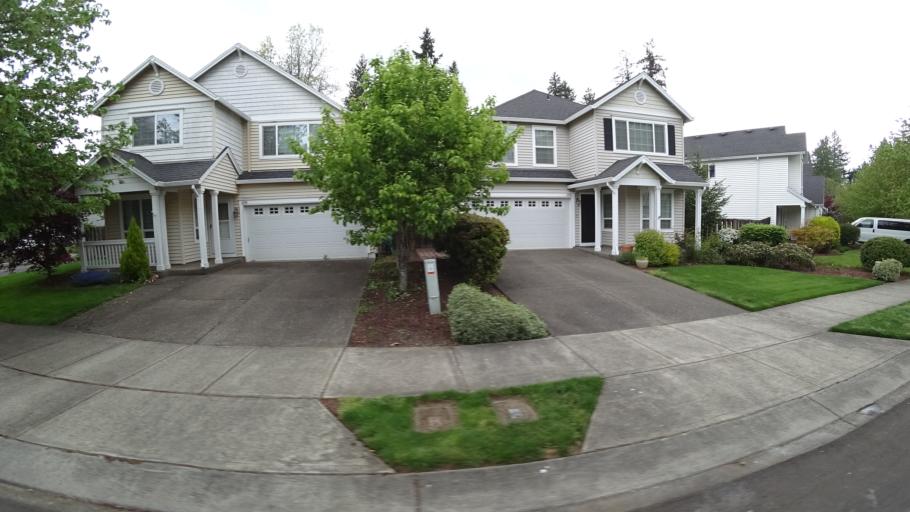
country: US
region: Oregon
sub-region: Washington County
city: Hillsboro
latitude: 45.5345
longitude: -122.9846
